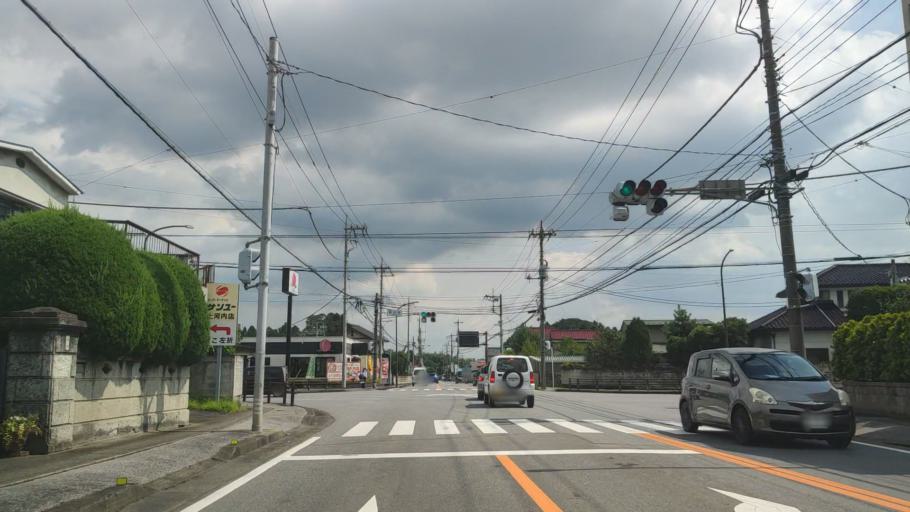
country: JP
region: Tochigi
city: Utsunomiya-shi
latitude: 36.6506
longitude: 139.8440
